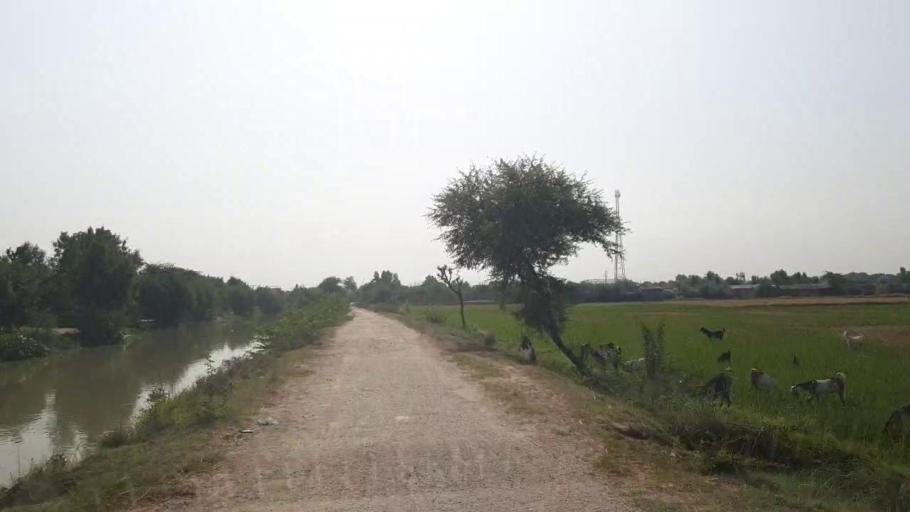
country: PK
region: Sindh
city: Badin
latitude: 24.6415
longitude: 68.8486
